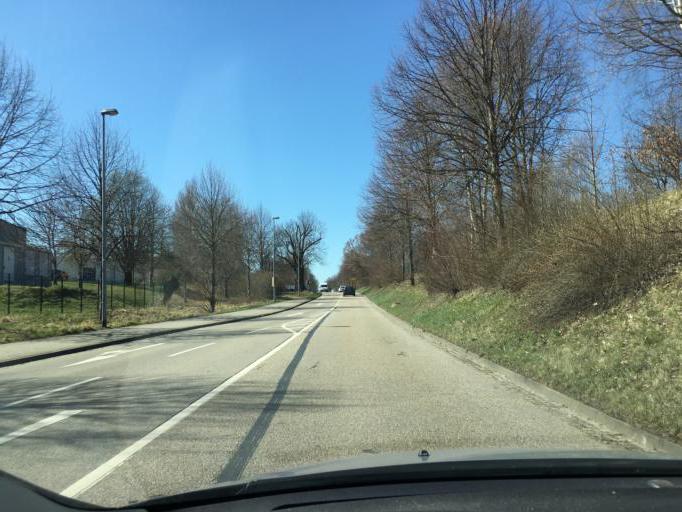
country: DE
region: Saxony
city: Limbach-Oberfrohna
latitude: 50.8600
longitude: 12.7795
